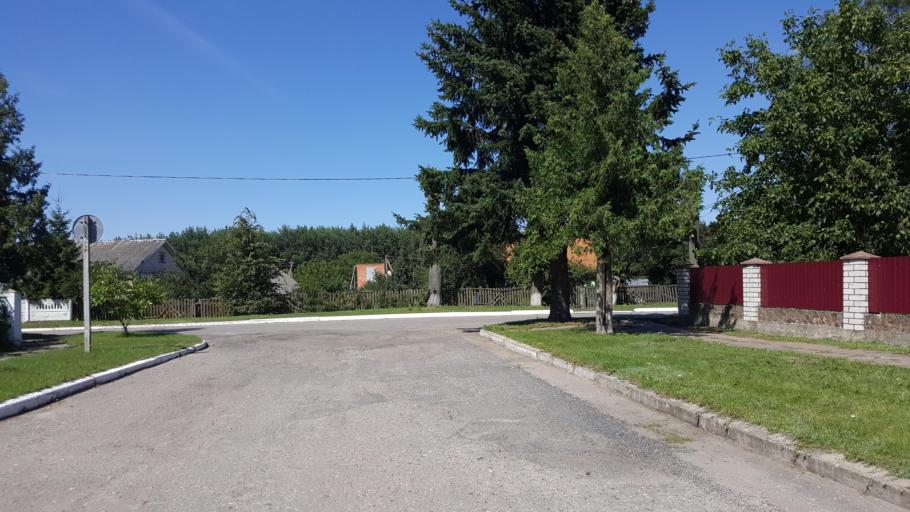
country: BY
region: Brest
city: Charnawchytsy
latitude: 52.2681
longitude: 23.5911
